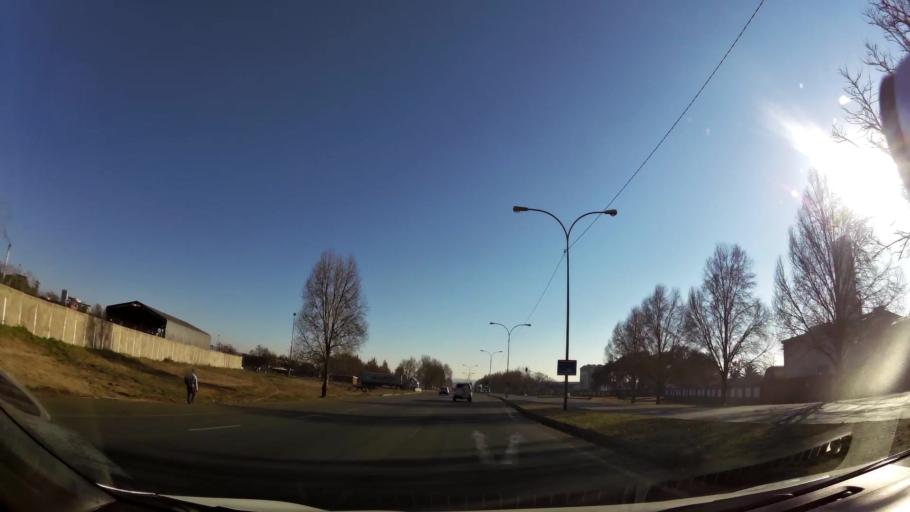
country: ZA
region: Gauteng
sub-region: Ekurhuleni Metropolitan Municipality
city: Germiston
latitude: -26.3147
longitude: 28.1395
